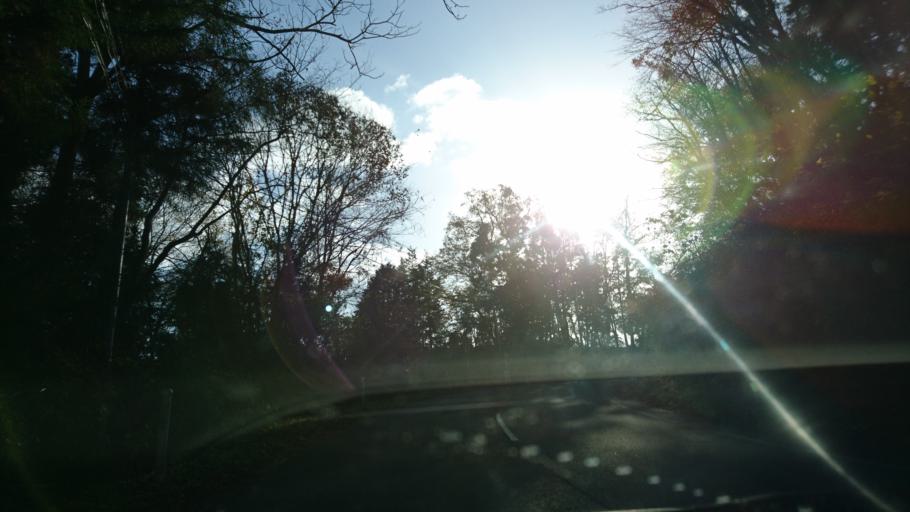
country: JP
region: Iwate
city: Ichinoseki
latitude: 38.8861
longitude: 141.2916
